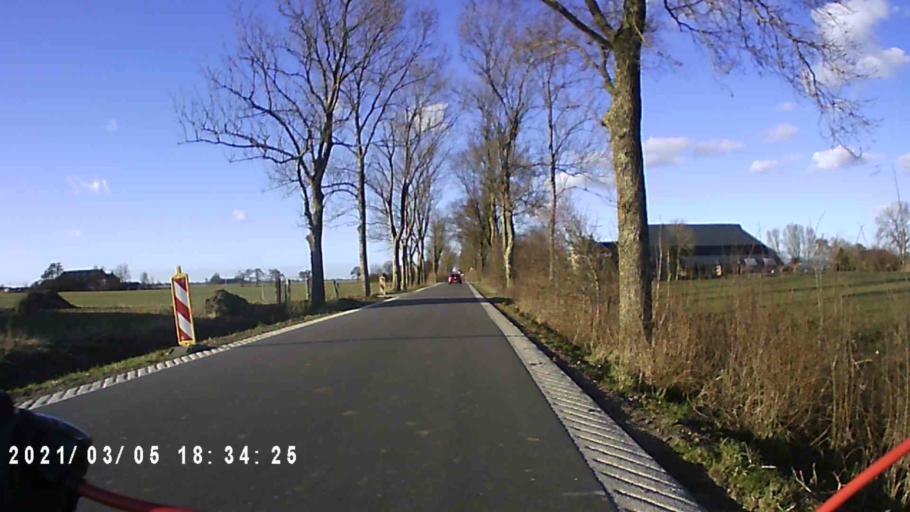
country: NL
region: Groningen
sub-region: Gemeente Groningen
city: Korrewegwijk
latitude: 53.2658
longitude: 6.5660
